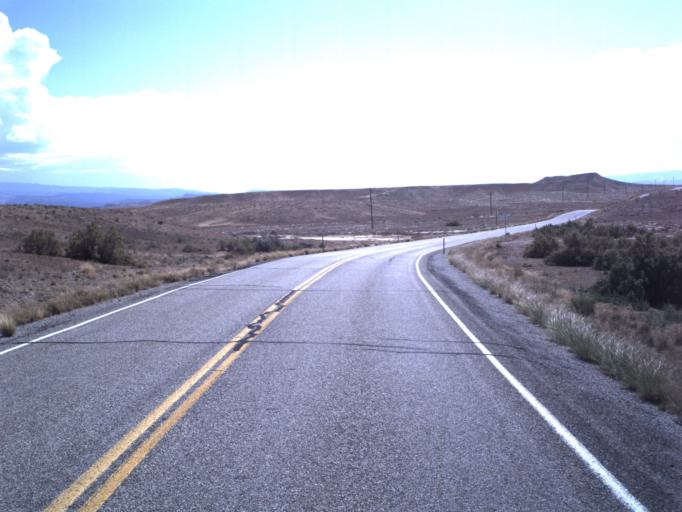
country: US
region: Utah
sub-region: Grand County
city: Moab
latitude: 38.9416
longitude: -109.3508
